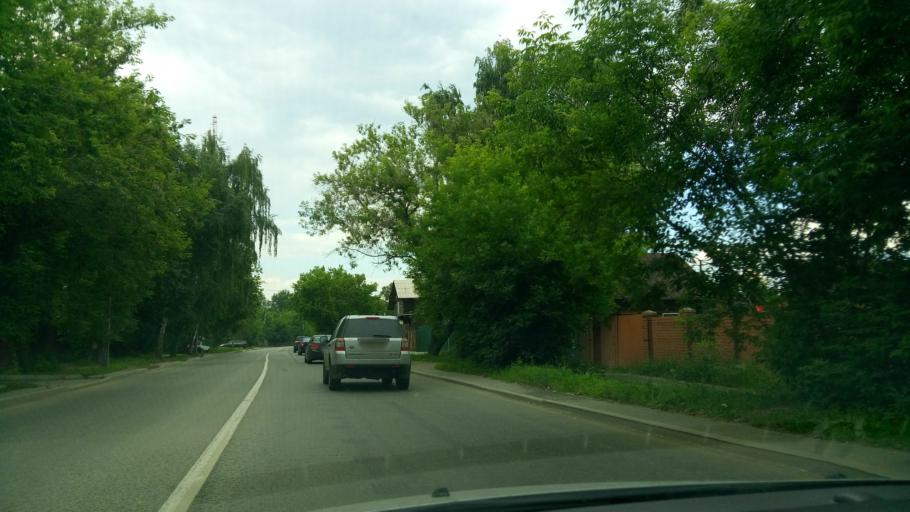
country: RU
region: Sverdlovsk
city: Yekaterinburg
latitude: 56.8796
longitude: 60.6928
